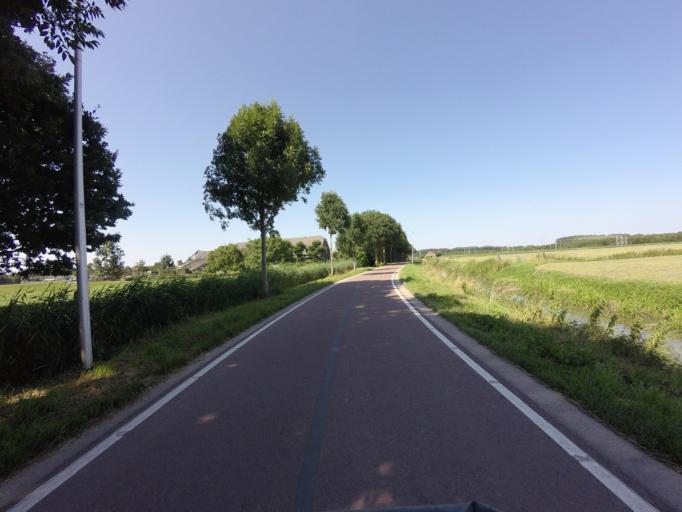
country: NL
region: Utrecht
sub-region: Gemeente Houten
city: Houten
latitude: 52.0464
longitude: 5.1546
